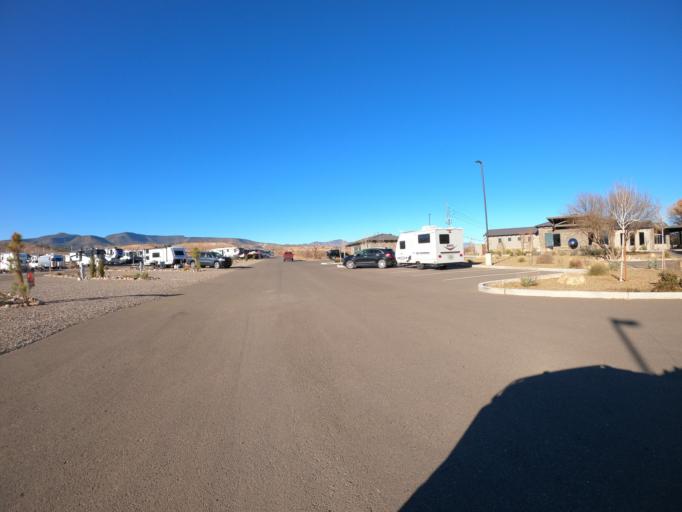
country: US
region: Arizona
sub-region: Yavapai County
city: Camp Verde
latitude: 34.5871
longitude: -111.8832
